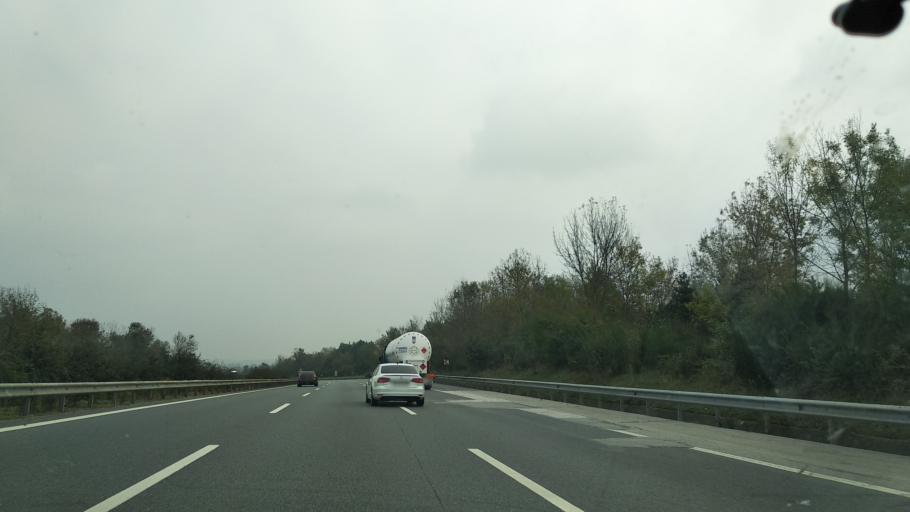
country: TR
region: Duzce
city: Gumusova
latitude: 40.8402
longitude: 30.9833
